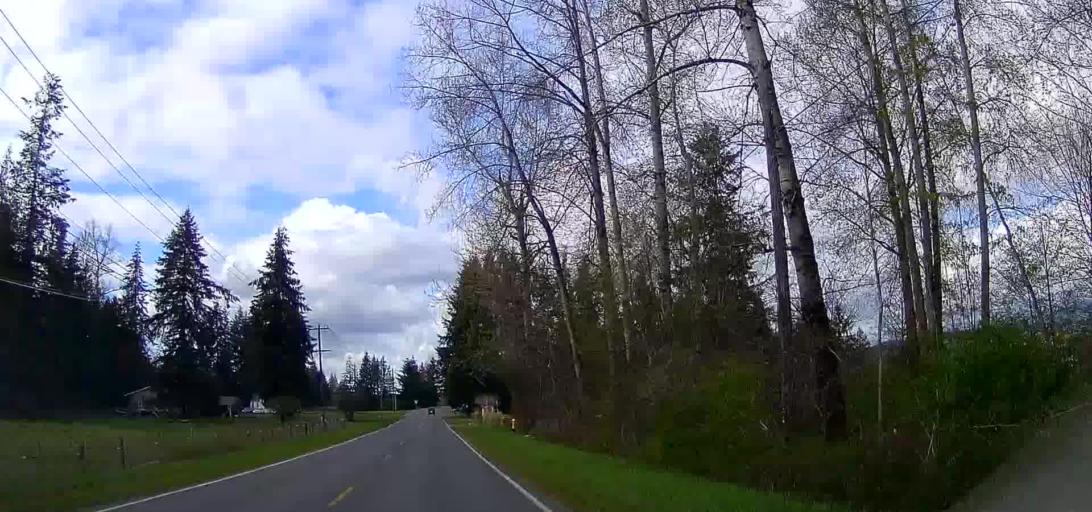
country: US
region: Washington
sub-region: Snohomish County
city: Smokey Point
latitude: 48.1726
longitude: -122.1899
